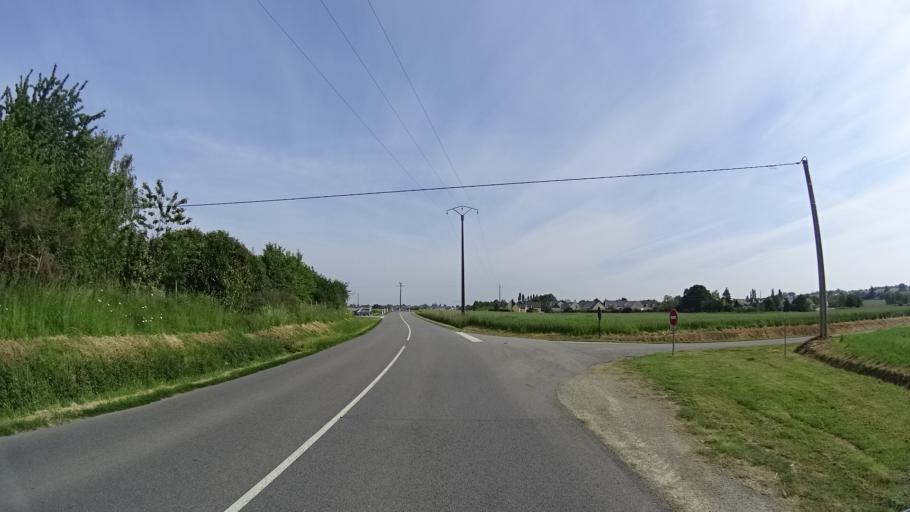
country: FR
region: Brittany
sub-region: Departement d'Ille-et-Vilaine
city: Chateaugiron
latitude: 48.0289
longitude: -1.5052
